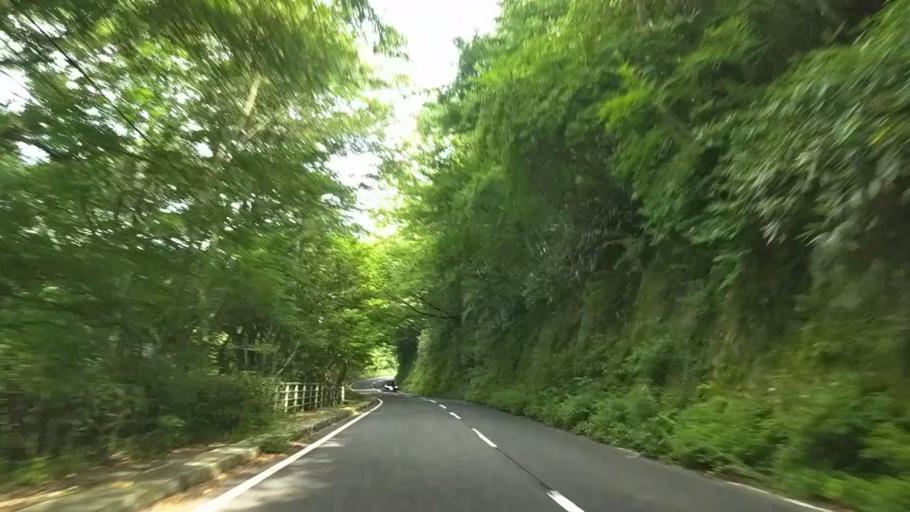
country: JP
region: Kanagawa
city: Hakone
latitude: 35.2529
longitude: 139.0225
